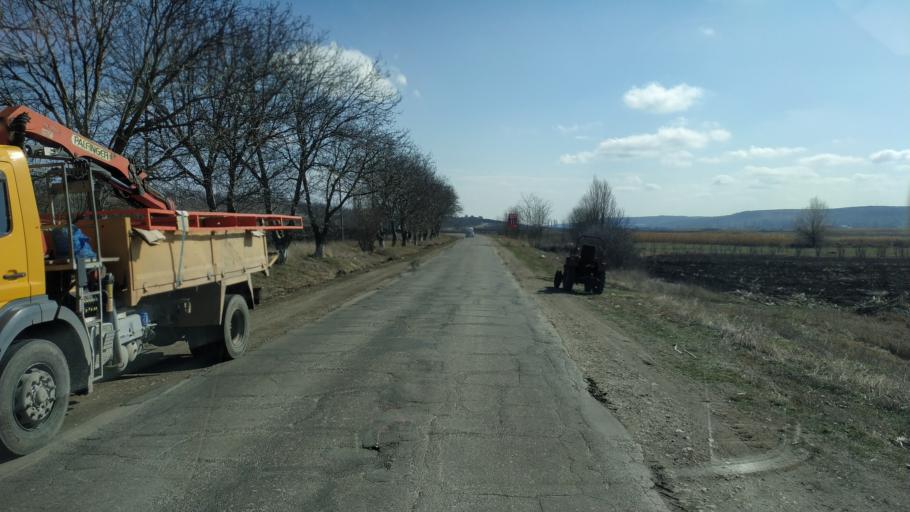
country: MD
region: Laloveni
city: Ialoveni
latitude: 46.9264
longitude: 28.6776
